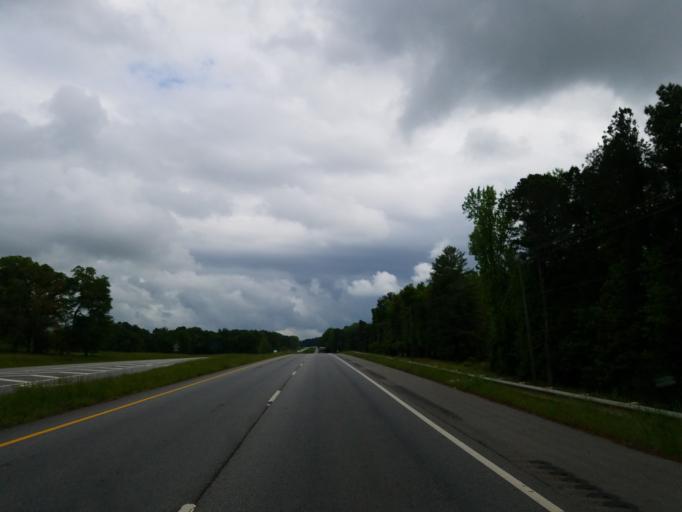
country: US
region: Georgia
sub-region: Spalding County
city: Griffin
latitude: 33.1610
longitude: -84.2566
